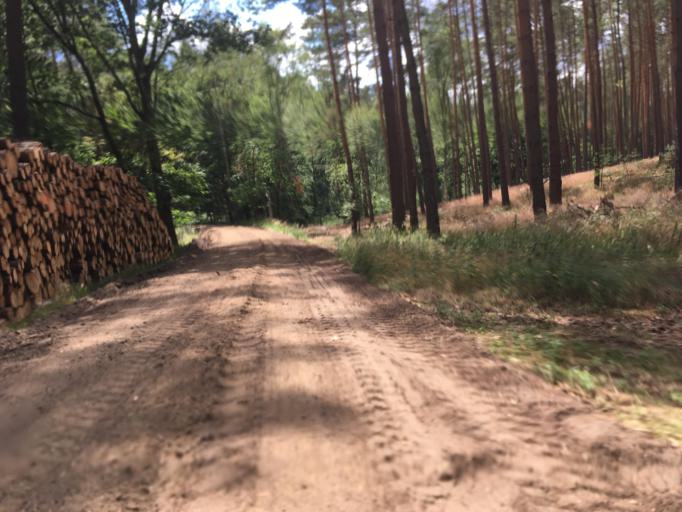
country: DE
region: Brandenburg
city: Joachimsthal
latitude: 52.9297
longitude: 13.7503
